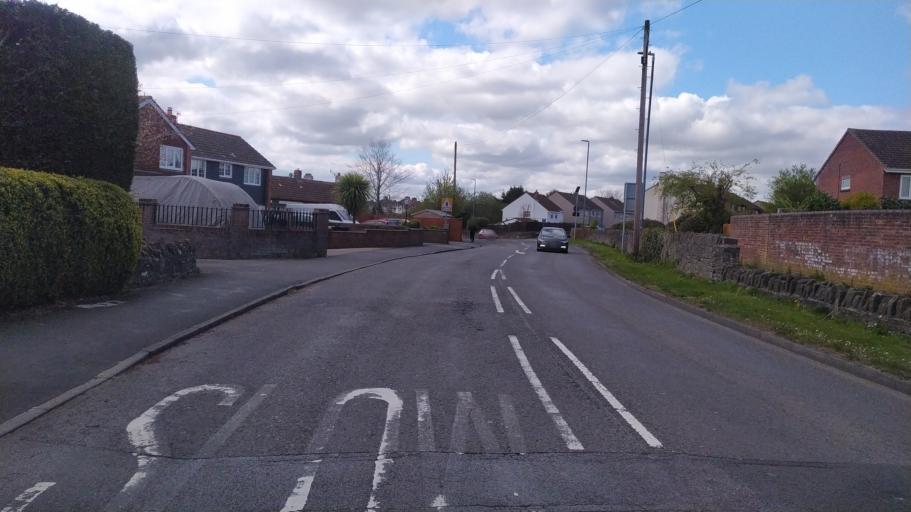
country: GB
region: England
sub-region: South Gloucestershire
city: Kingswood
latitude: 51.4447
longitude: -2.4887
